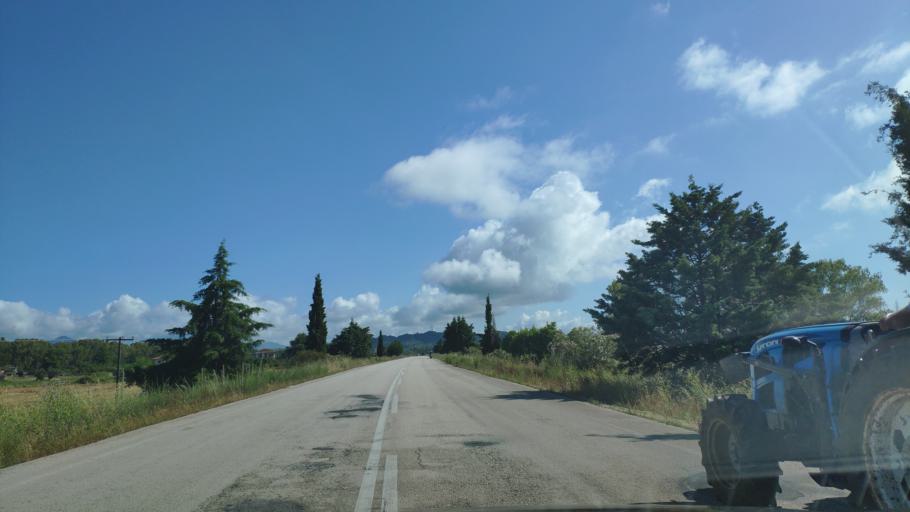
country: GR
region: Epirus
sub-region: Nomos Prevezis
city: Preveza
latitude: 38.9969
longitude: 20.7149
